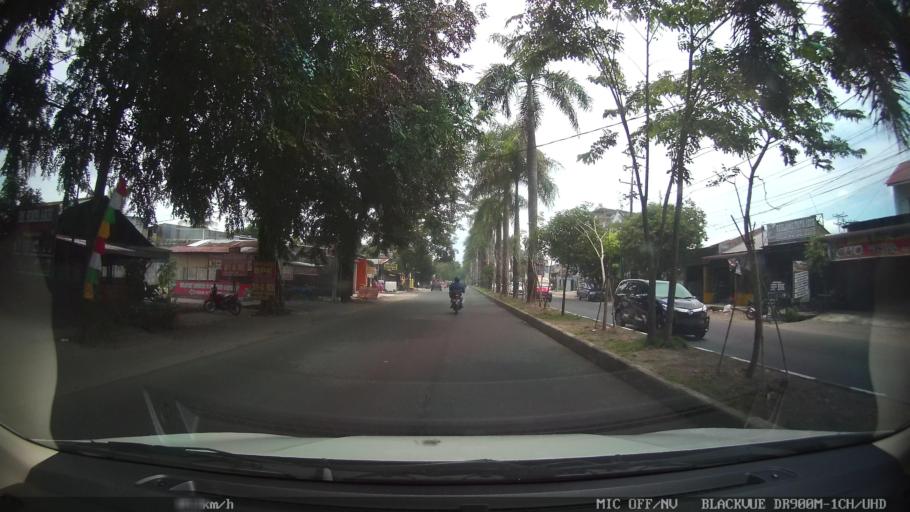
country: ID
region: North Sumatra
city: Sunggal
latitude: 3.5223
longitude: 98.6240
